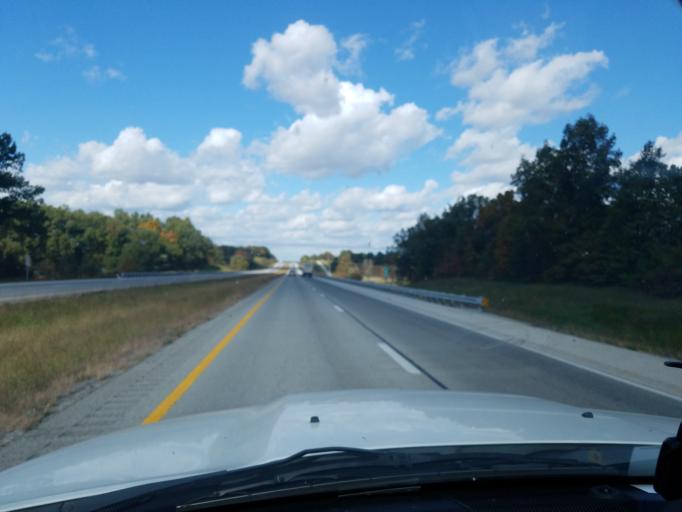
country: US
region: Kentucky
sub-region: Daviess County
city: Masonville
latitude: 37.6256
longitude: -86.9881
